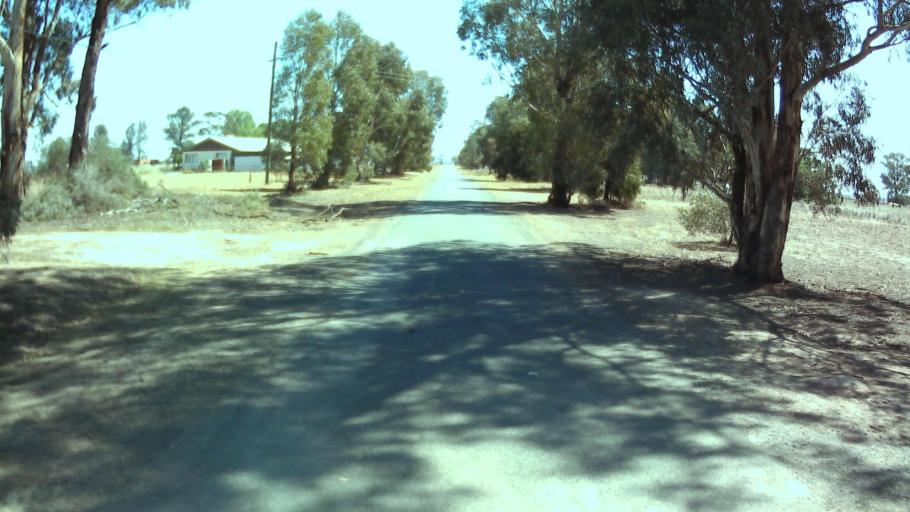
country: AU
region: New South Wales
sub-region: Weddin
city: Grenfell
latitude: -33.8417
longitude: 147.7409
